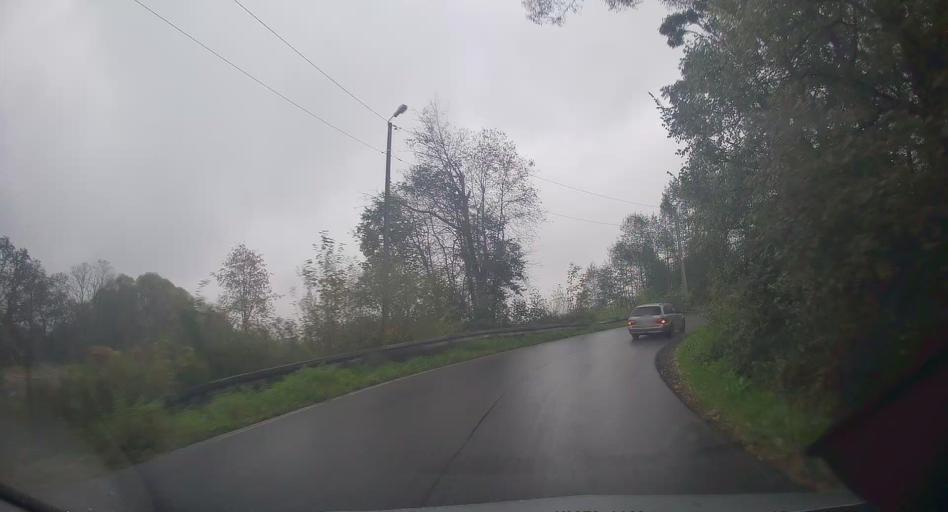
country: PL
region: Lesser Poland Voivodeship
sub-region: Powiat krakowski
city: Ochojno
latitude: 49.9635
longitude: 20.0022
